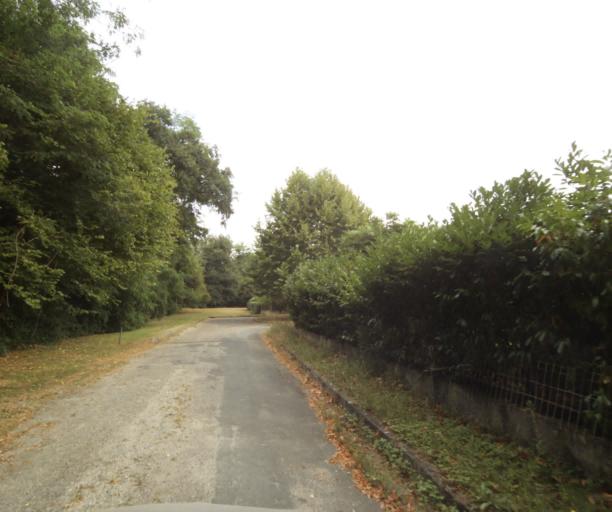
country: FR
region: Aquitaine
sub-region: Departement de la Gironde
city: Creon
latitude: 44.7691
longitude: -0.3401
